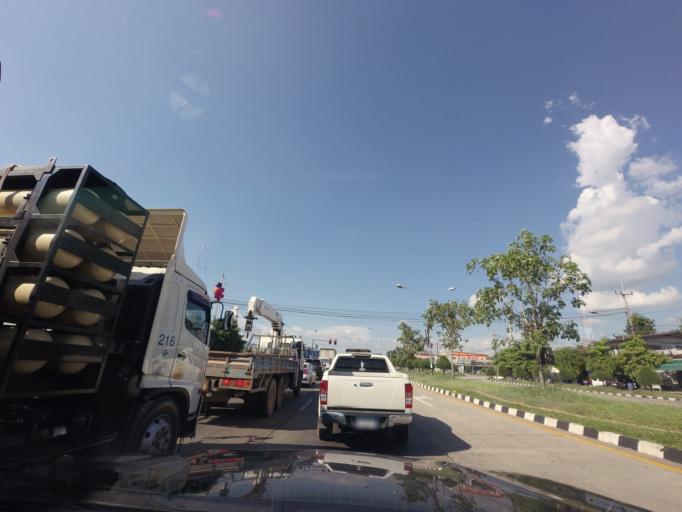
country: TH
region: Nakhon Ratchasima
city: Sida
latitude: 15.5465
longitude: 102.5477
